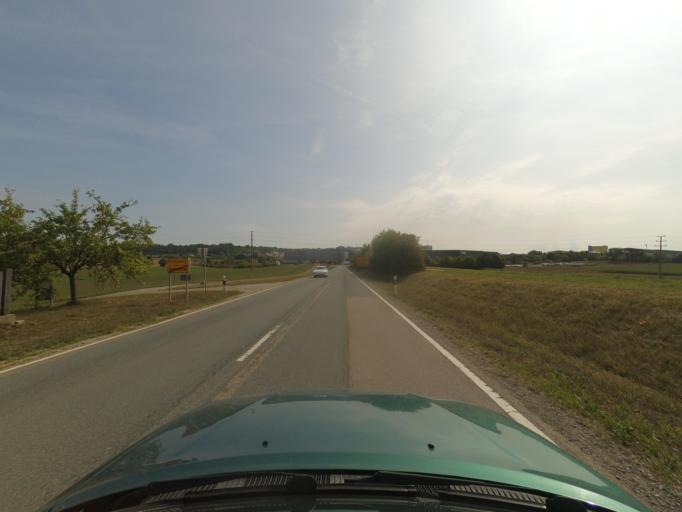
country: DE
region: Bavaria
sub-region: Regierungsbezirk Mittelfranken
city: Feuchtwangen
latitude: 49.1716
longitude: 10.3078
